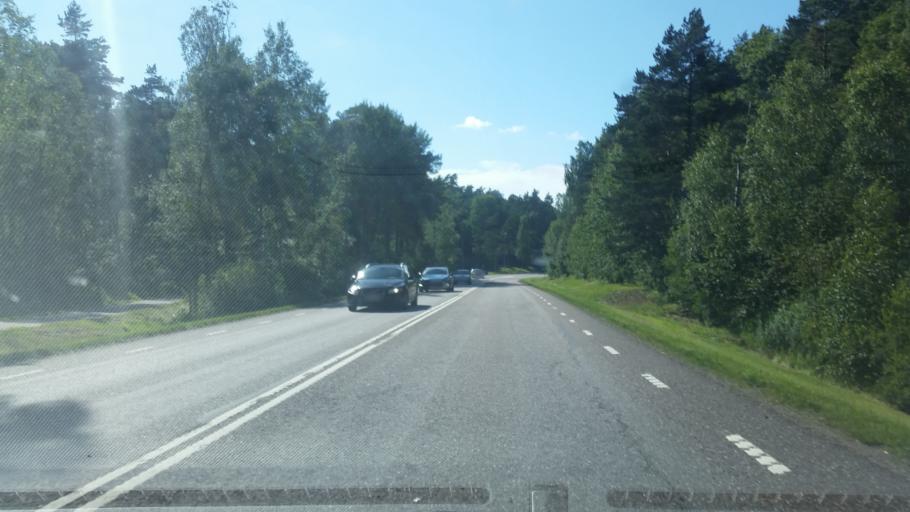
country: SE
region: Vaestra Goetaland
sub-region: Partille Kommun
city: Furulund
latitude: 57.7259
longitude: 12.1236
